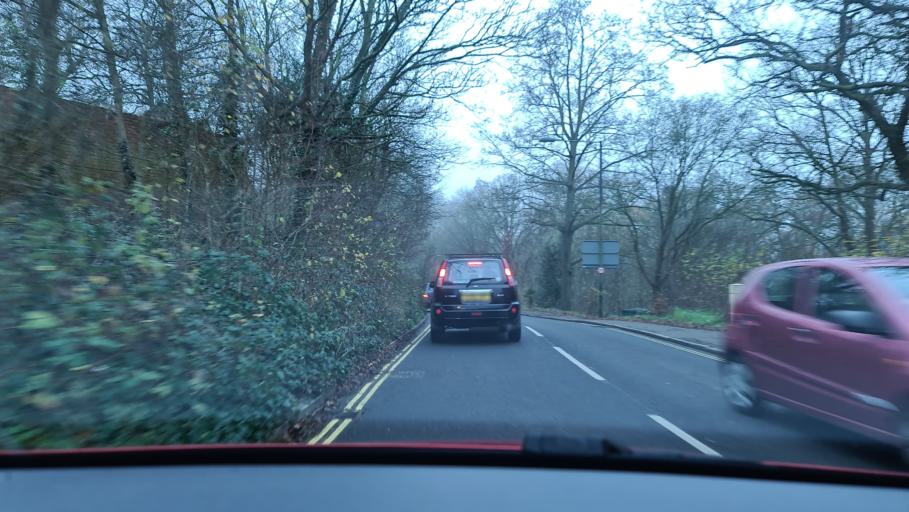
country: GB
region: England
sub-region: Greater London
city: Richmond
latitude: 51.4501
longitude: -0.2965
